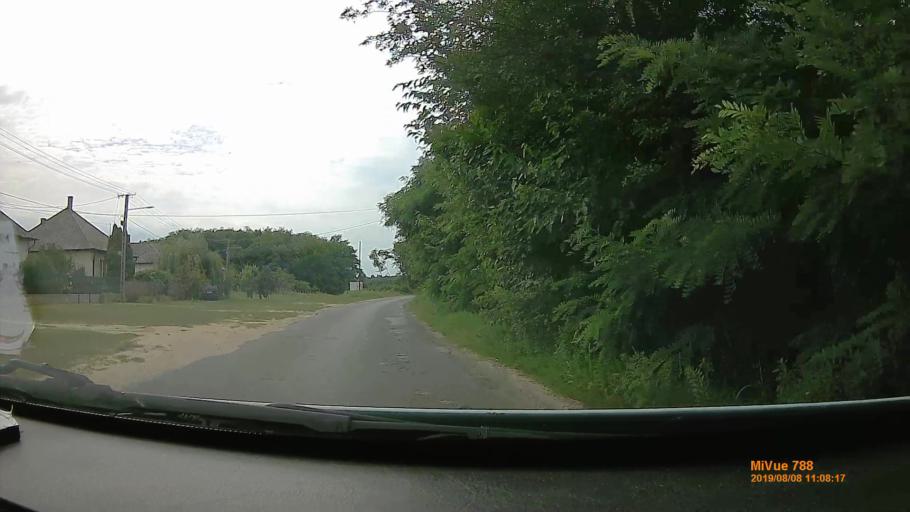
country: HU
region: Szabolcs-Szatmar-Bereg
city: Balkany
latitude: 47.7597
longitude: 21.8482
